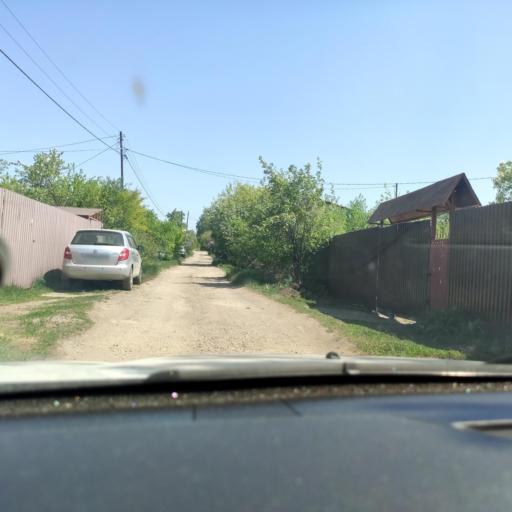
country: RU
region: Samara
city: Petra-Dubrava
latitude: 53.2775
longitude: 50.3267
